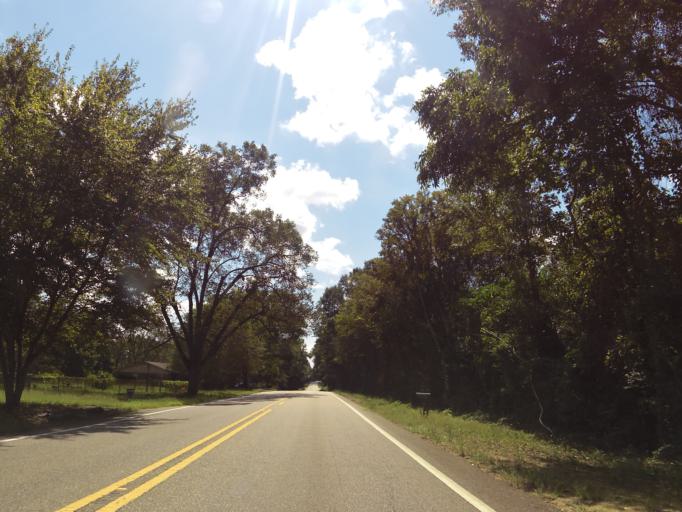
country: US
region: Alabama
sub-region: Dallas County
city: Selma
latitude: 32.4757
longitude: -87.0927
